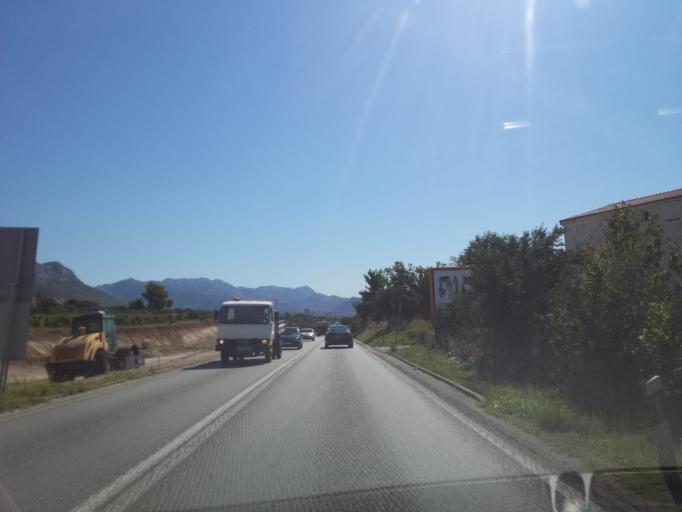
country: HR
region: Splitsko-Dalmatinska
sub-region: Grad Split
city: Split
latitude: 43.5550
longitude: 16.3983
